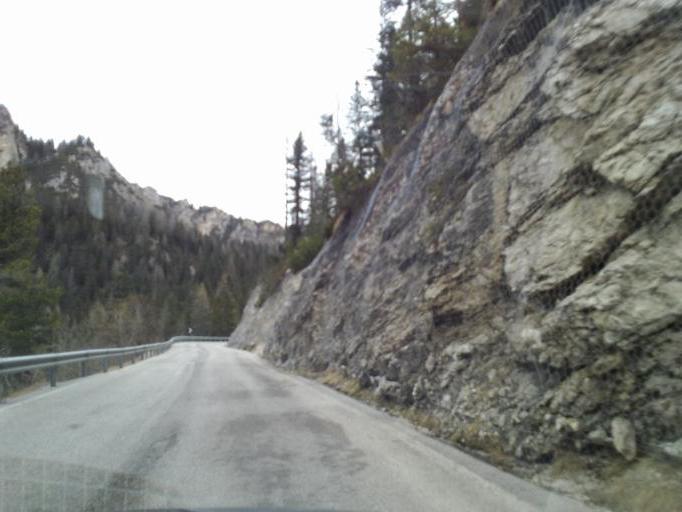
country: IT
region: Veneto
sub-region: Provincia di Belluno
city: Cortina d'Ampezzo
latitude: 46.5993
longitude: 12.2447
